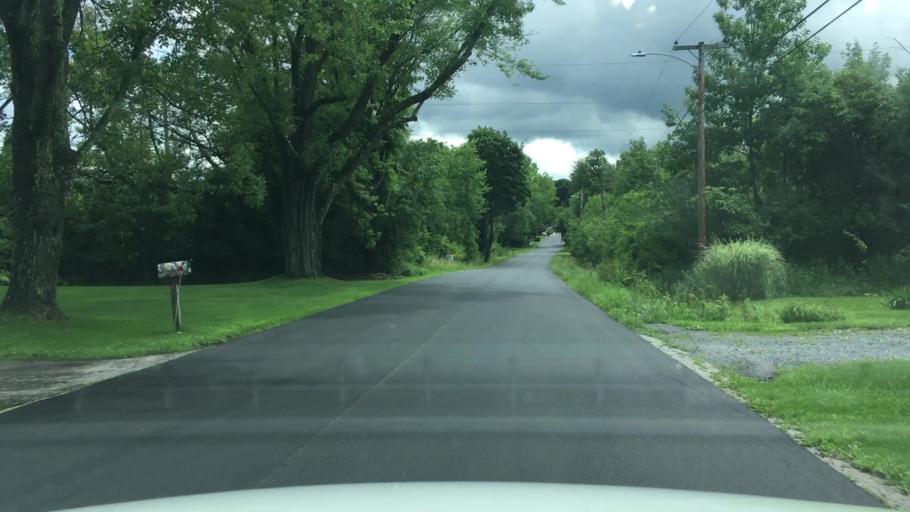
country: US
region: Vermont
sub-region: Bennington County
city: Bennington
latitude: 42.8861
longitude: -73.2069
